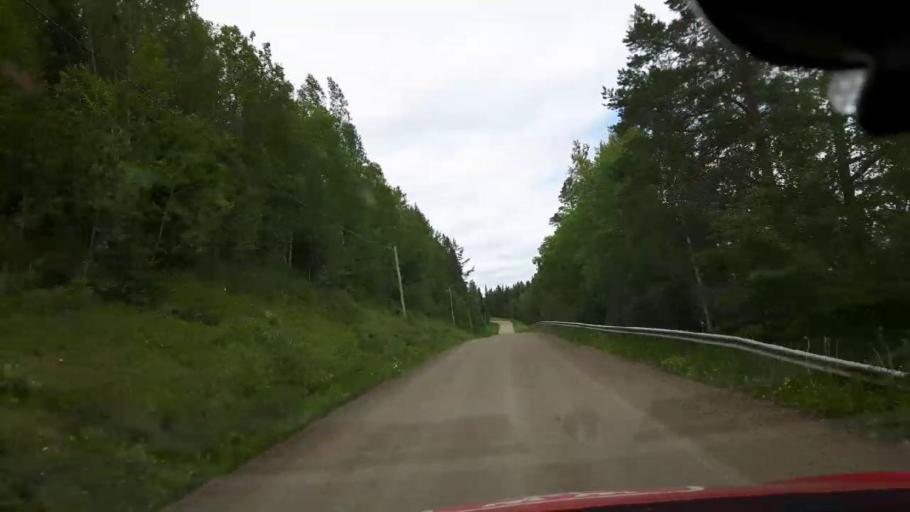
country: SE
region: Jaemtland
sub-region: OEstersunds Kommun
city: Brunflo
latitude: 62.9028
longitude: 15.1111
